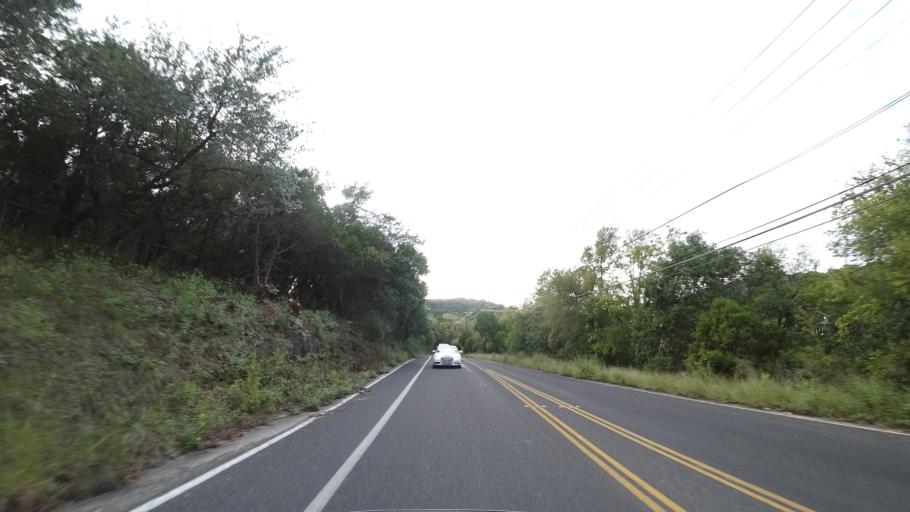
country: US
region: Texas
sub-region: Travis County
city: West Lake Hills
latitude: 30.2915
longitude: -97.7956
